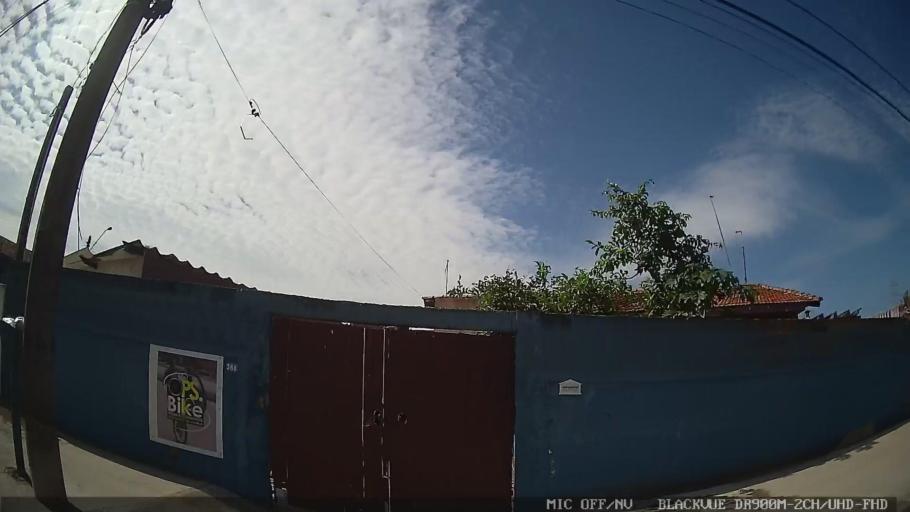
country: BR
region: Sao Paulo
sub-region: Itanhaem
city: Itanhaem
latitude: -24.1539
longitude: -46.7422
